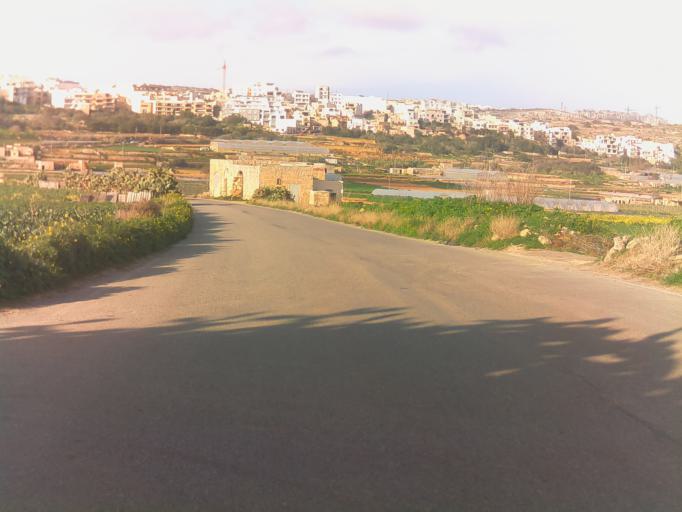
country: MT
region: L-Imgarr
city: Imgarr
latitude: 35.9331
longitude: 14.3511
